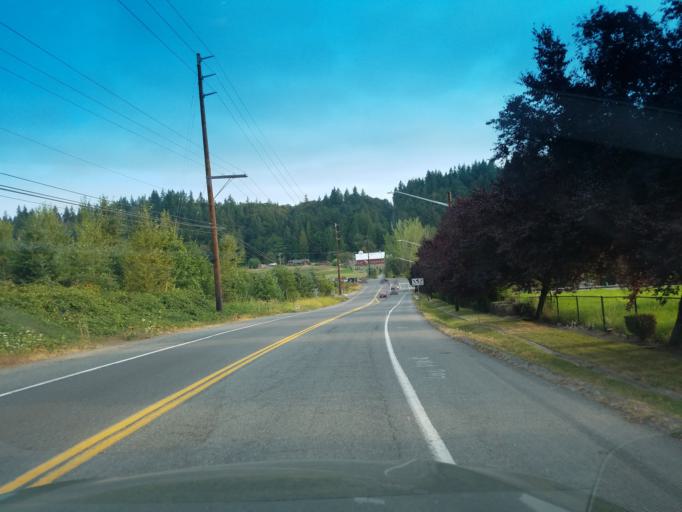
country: US
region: Washington
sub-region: King County
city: Sammamish
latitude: 47.6541
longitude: -122.0627
